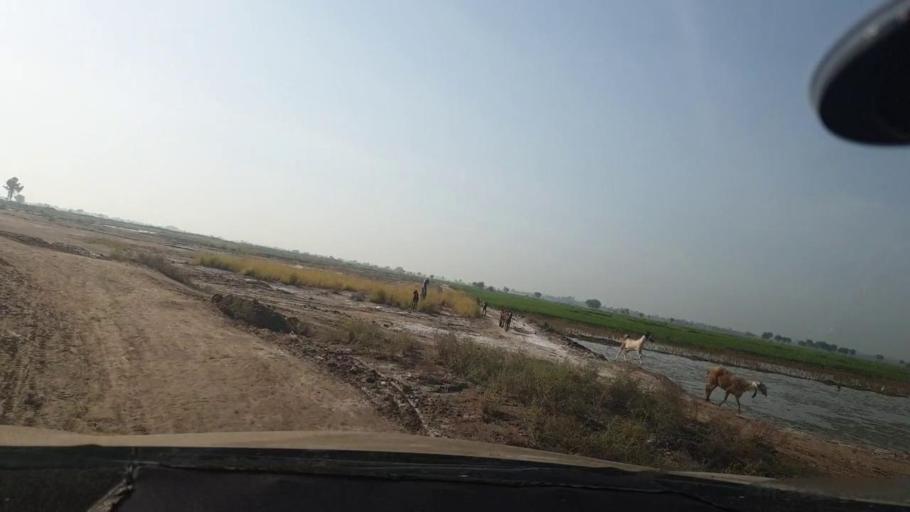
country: PK
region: Sindh
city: Kambar
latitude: 27.6419
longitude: 68.0496
